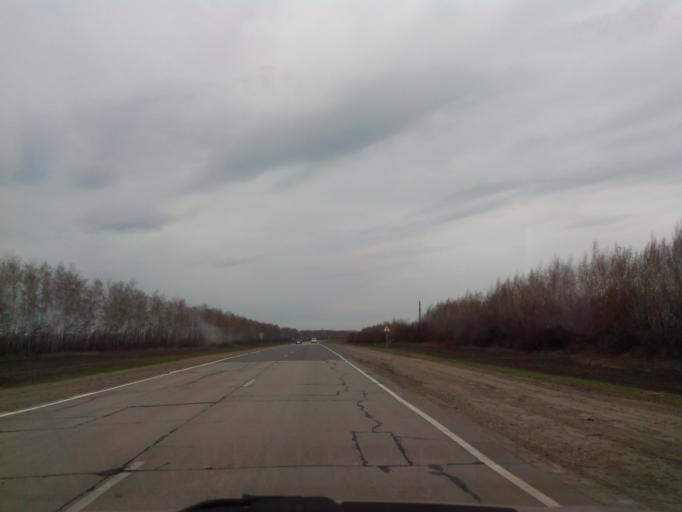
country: RU
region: Tambov
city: Znamenka
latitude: 52.4064
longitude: 41.3863
